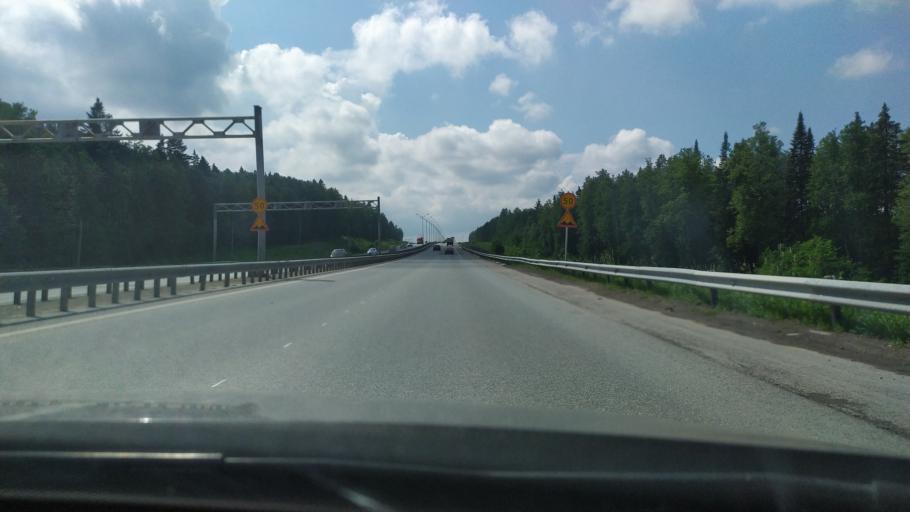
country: RU
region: Perm
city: Ferma
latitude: 58.0100
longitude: 56.3992
